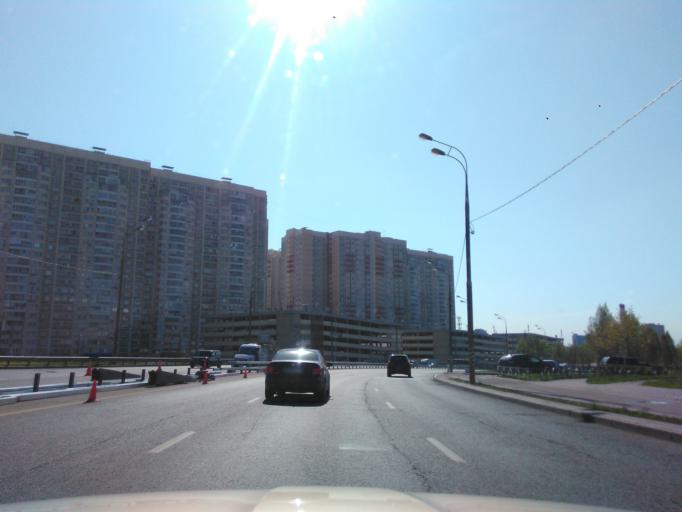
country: RU
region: Moscow
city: Khimki
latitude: 55.9011
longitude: 37.3969
